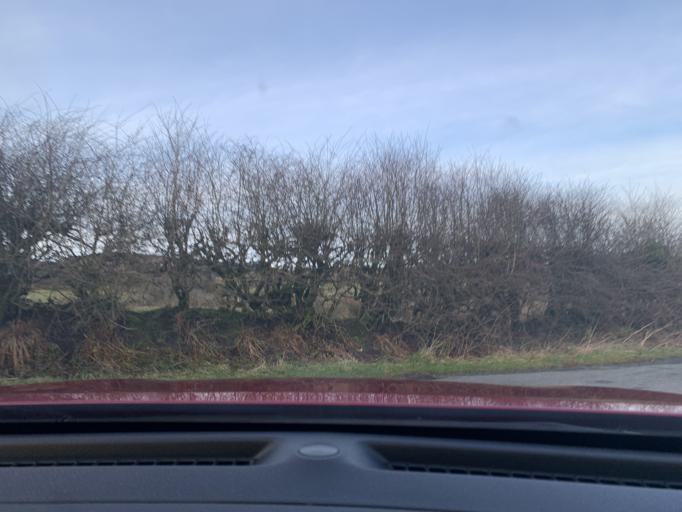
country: IE
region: Connaught
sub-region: Sligo
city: Strandhill
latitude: 54.1756
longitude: -8.6570
